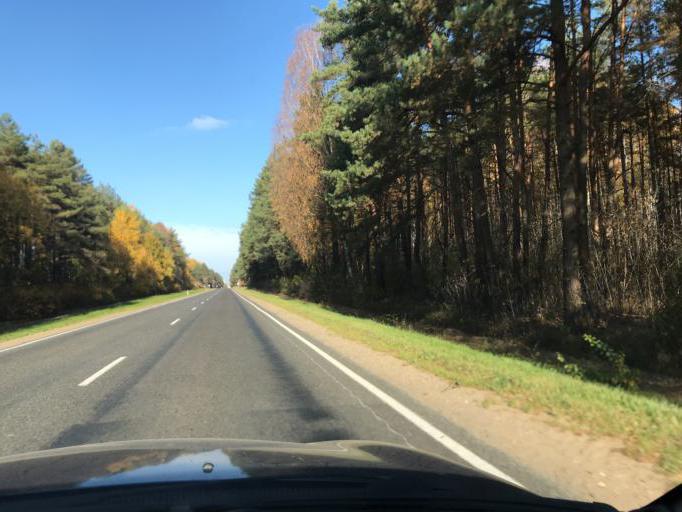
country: BY
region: Grodnenskaya
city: Lida
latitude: 53.9689
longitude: 25.2339
